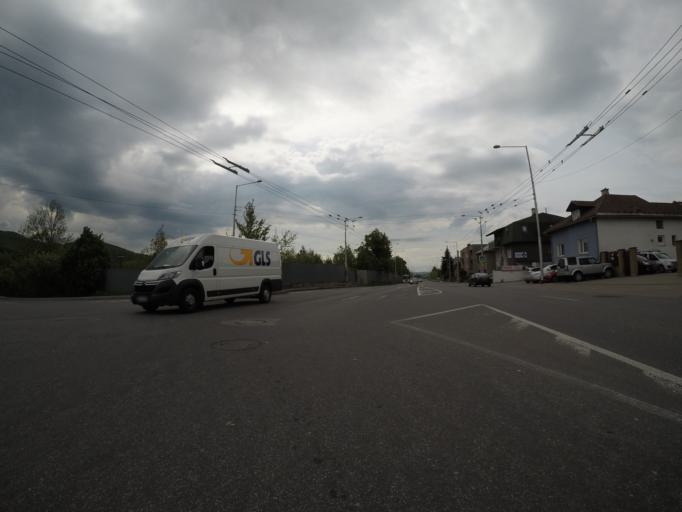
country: SK
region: Banskobystricky
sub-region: Okres Banska Bystrica
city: Banska Bystrica
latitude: 48.7169
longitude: 19.1324
